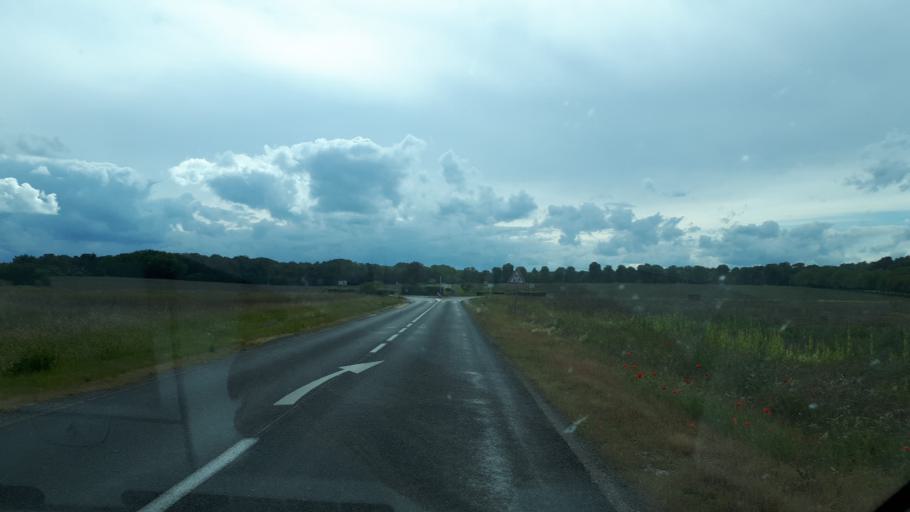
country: FR
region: Centre
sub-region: Departement du Cher
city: Mehun-sur-Yevre
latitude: 47.0782
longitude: 2.1826
